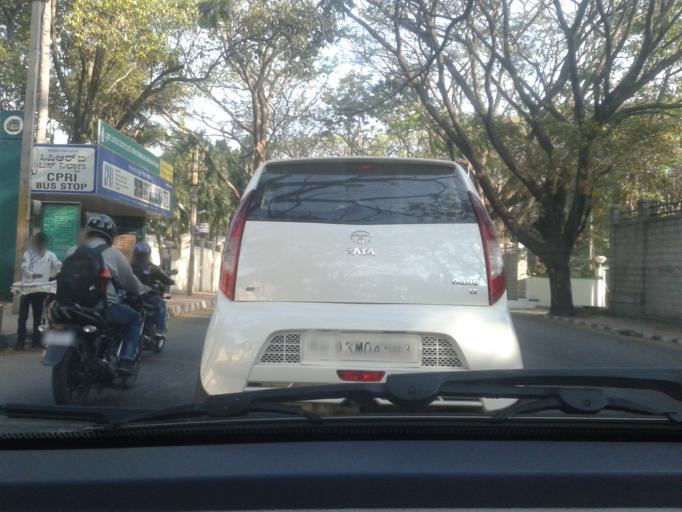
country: IN
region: Karnataka
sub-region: Bangalore Urban
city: Bangalore
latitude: 13.0218
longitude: 77.5723
